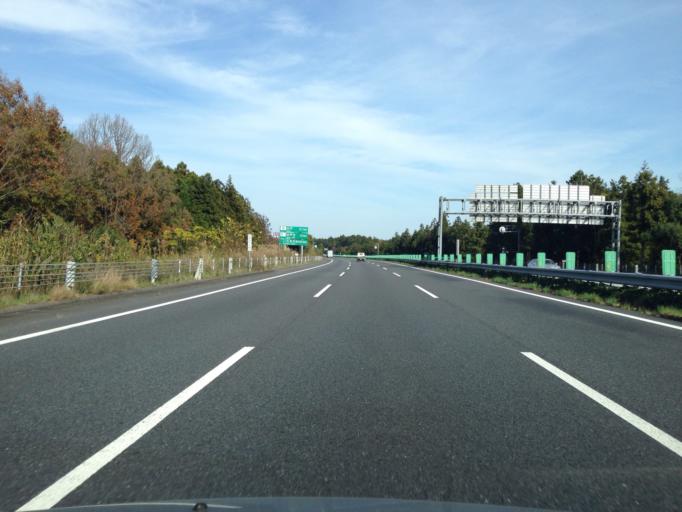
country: JP
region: Ibaraki
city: Tomobe
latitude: 36.3299
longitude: 140.3551
